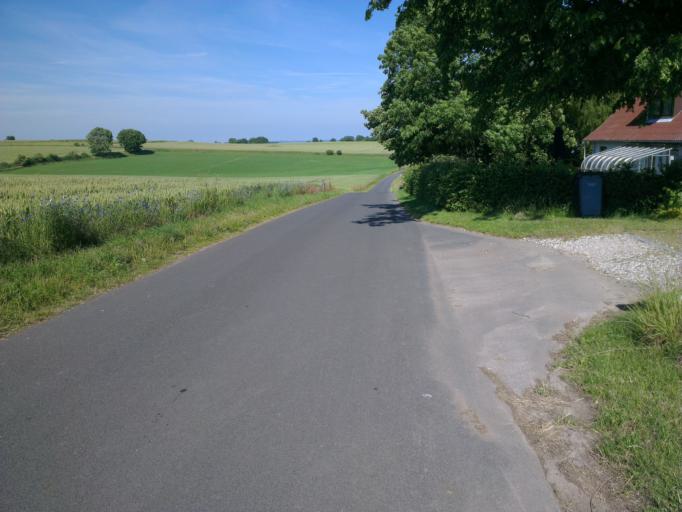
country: DK
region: Capital Region
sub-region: Frederikssund Kommune
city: Skibby
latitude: 55.7848
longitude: 11.8801
